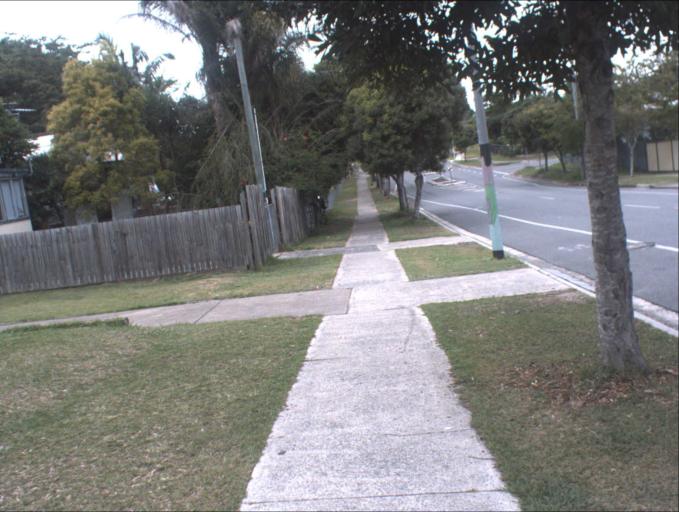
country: AU
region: Queensland
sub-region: Logan
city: Woodridge
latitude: -27.6309
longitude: 153.1033
